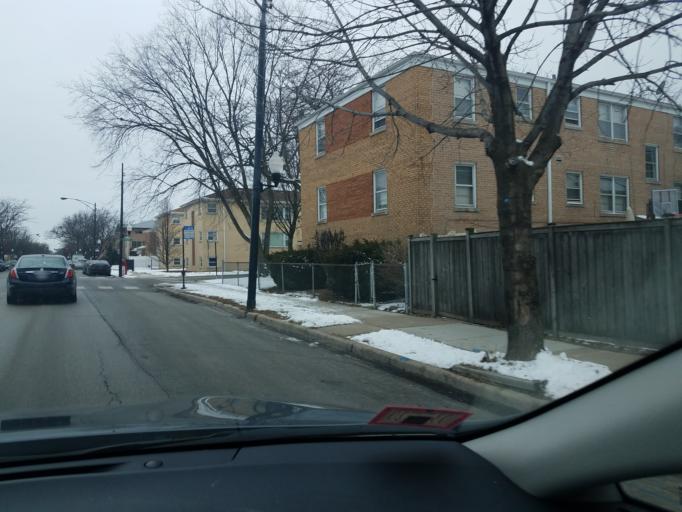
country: US
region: Illinois
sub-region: Cook County
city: Harwood Heights
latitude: 41.9604
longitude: -87.7790
